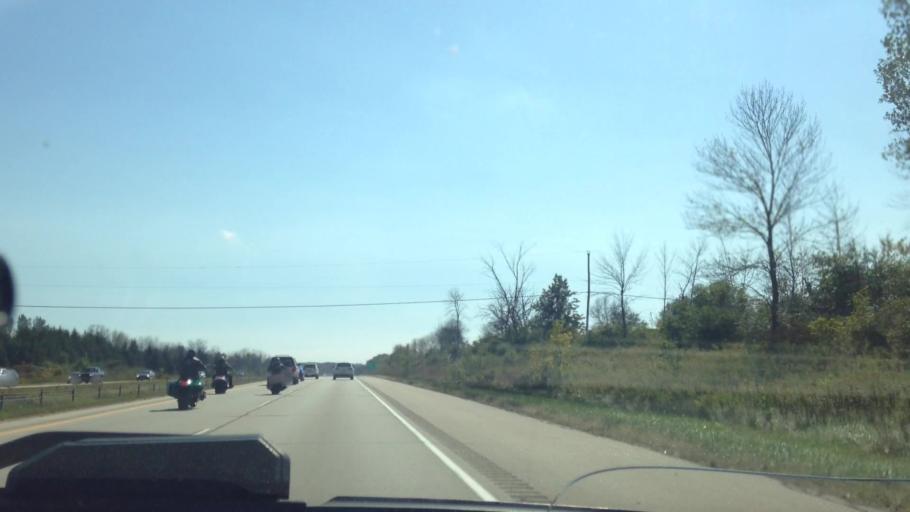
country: US
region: Wisconsin
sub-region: Ozaukee County
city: Thiensville
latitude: 43.2440
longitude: -87.9201
